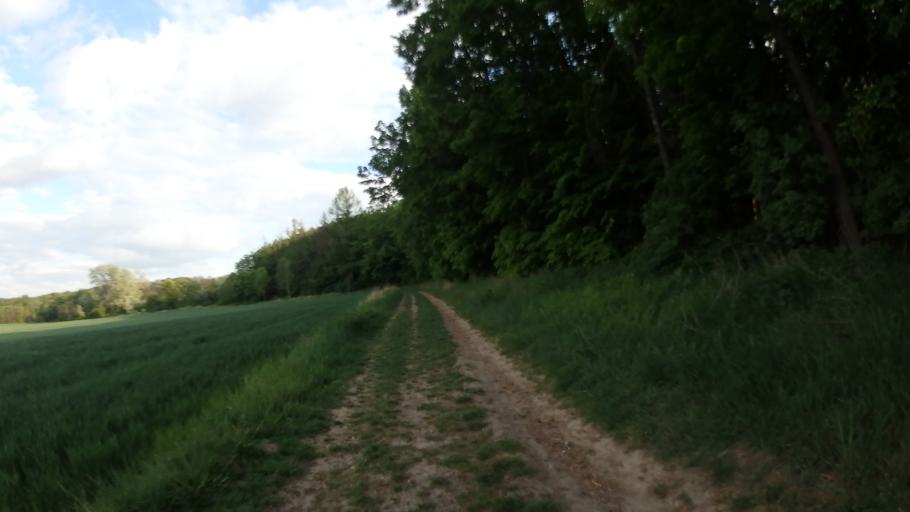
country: CZ
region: South Moravian
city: Moravany
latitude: 49.1363
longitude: 16.5690
